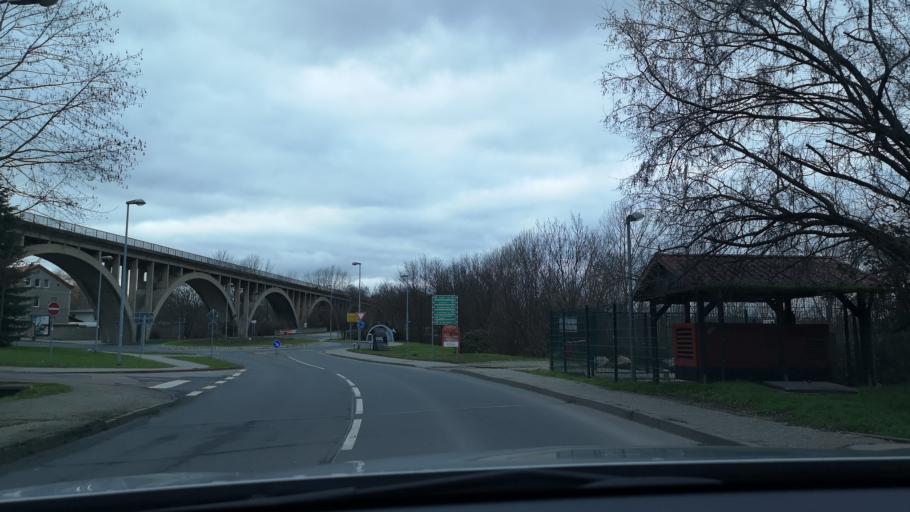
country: DE
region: Saxony-Anhalt
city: Mucheln
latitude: 51.3047
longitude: 11.8129
